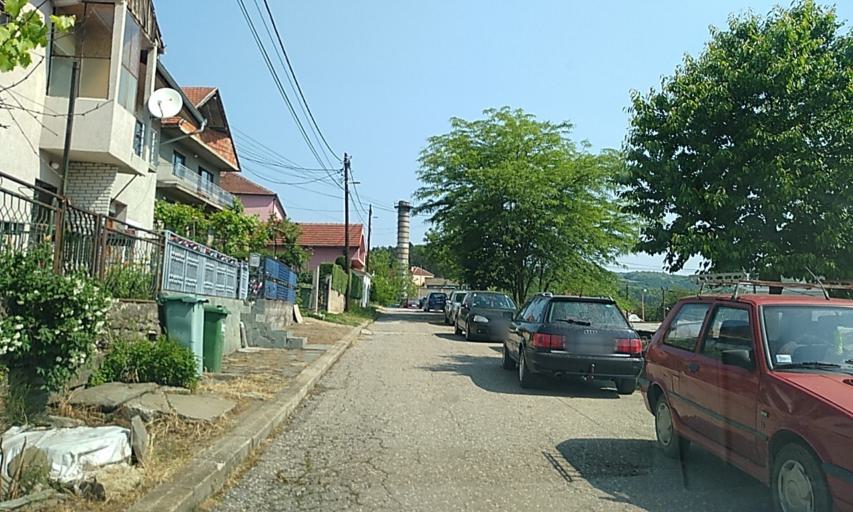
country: RS
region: Central Serbia
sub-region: Pcinjski Okrug
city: Vladicin Han
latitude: 42.7142
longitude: 22.0633
